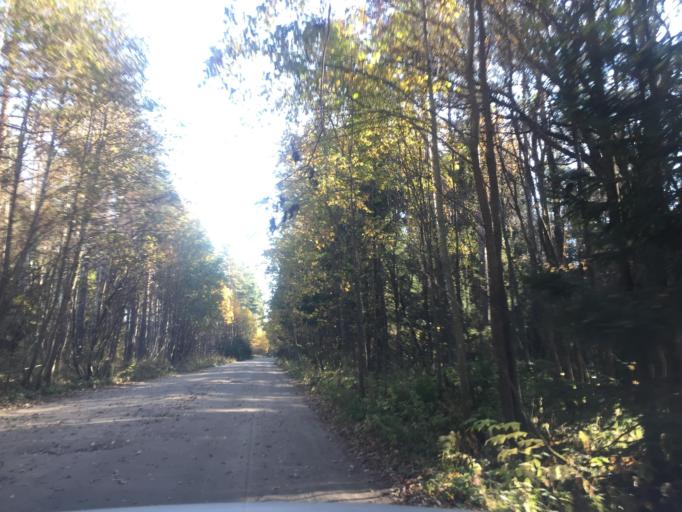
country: RU
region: Leningrad
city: Kuznechnoye
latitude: 61.3044
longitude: 30.0433
